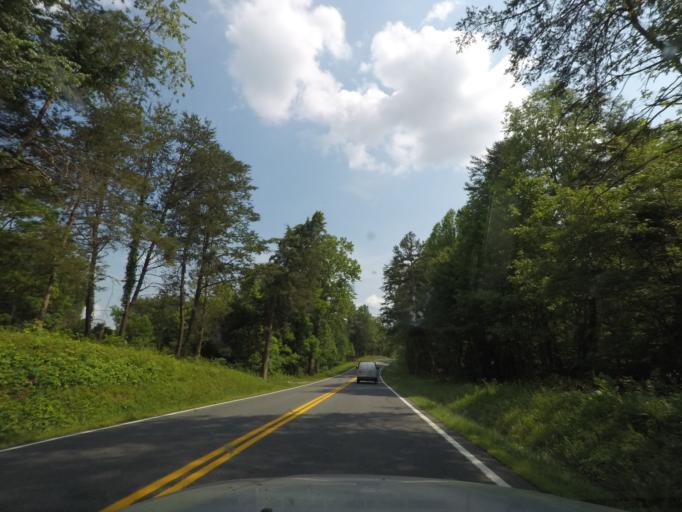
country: US
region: Virginia
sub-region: Fluvanna County
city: Palmyra
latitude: 37.8847
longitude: -78.2625
